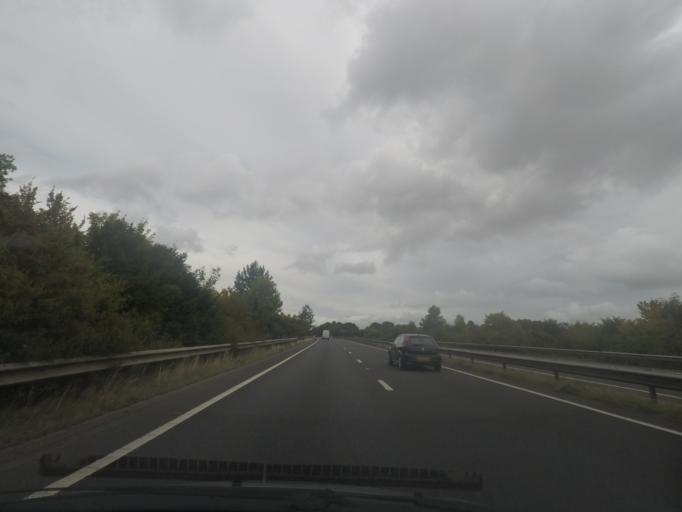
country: GB
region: England
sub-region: Wiltshire
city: Tidworth
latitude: 51.1938
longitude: -1.6559
